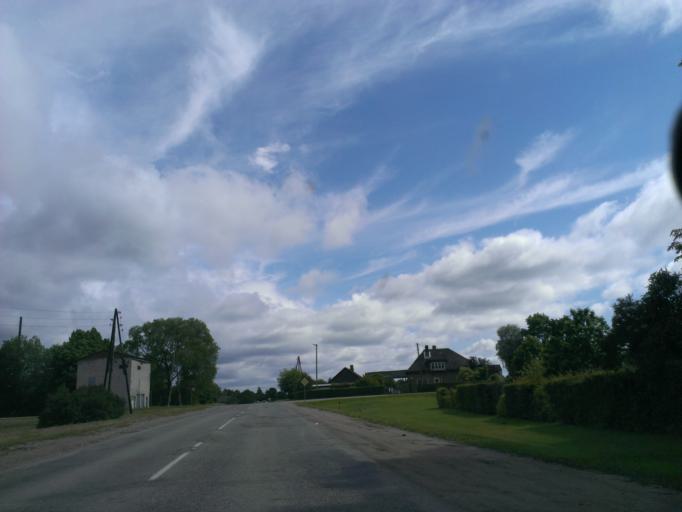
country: LV
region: Grobina
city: Grobina
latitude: 56.5379
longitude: 21.1541
